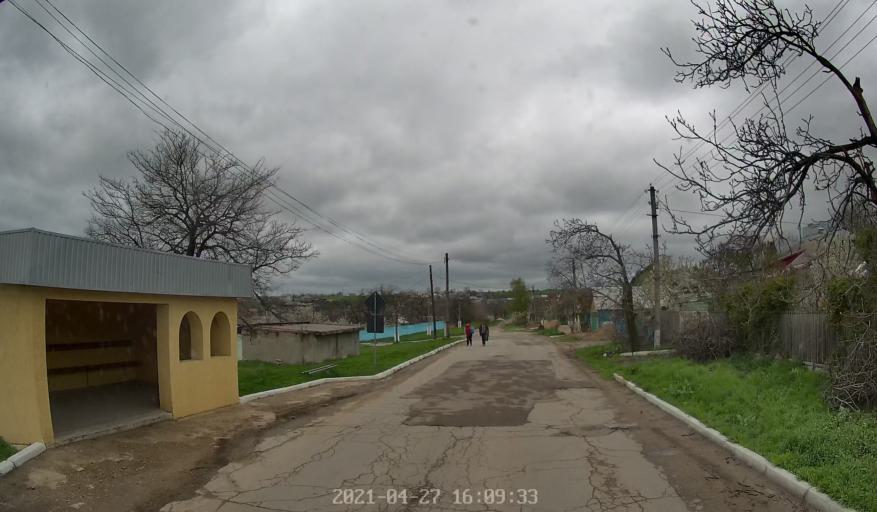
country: MD
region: Chisinau
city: Vadul lui Voda
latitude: 47.0112
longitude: 29.0161
